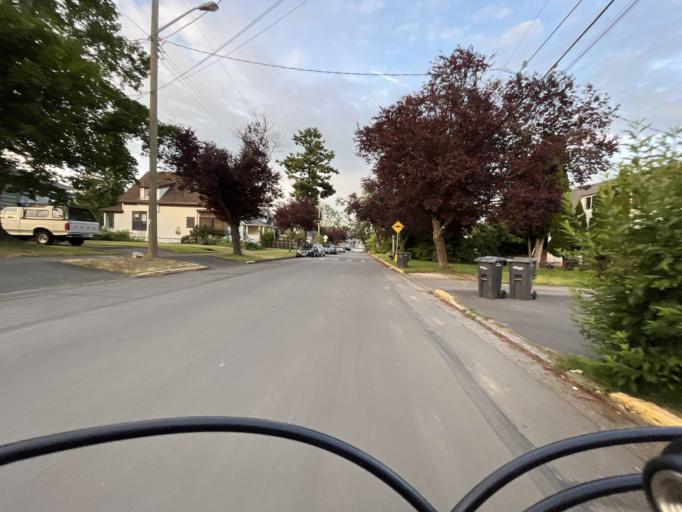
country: CA
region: British Columbia
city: Victoria
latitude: 48.4310
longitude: -123.3962
